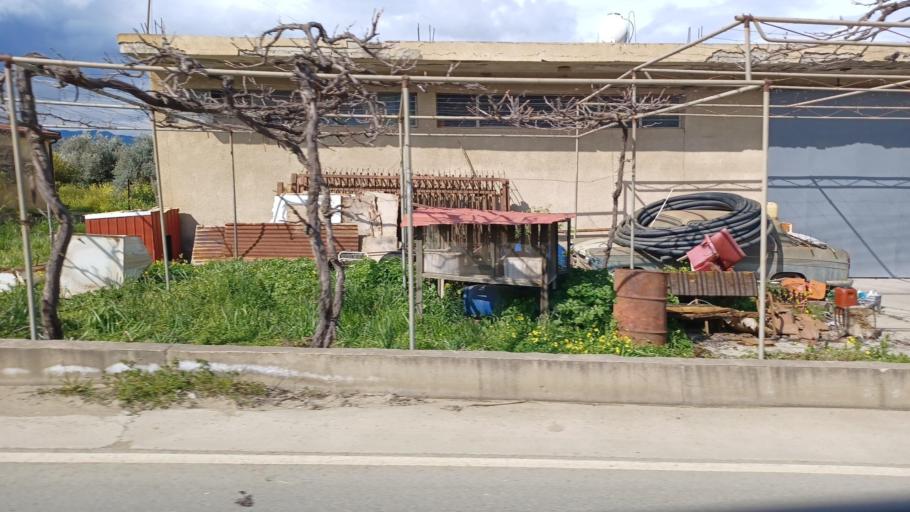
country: CY
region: Lefkosia
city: Lefka
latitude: 35.0878
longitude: 32.8890
